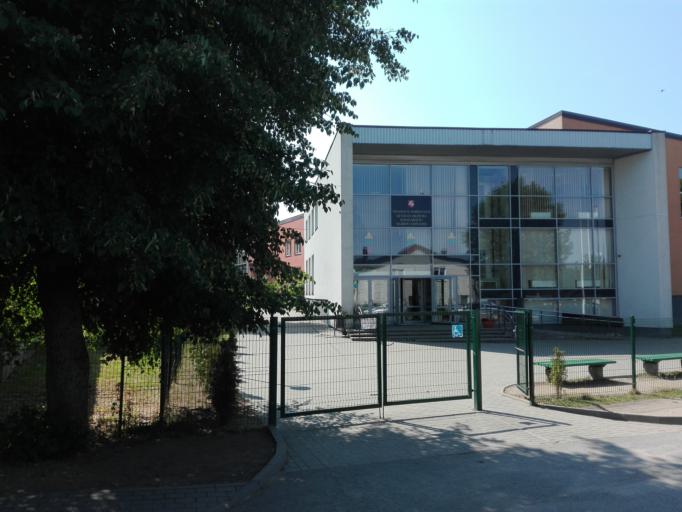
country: LT
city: Grigiskes
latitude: 54.8693
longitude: 25.0637
